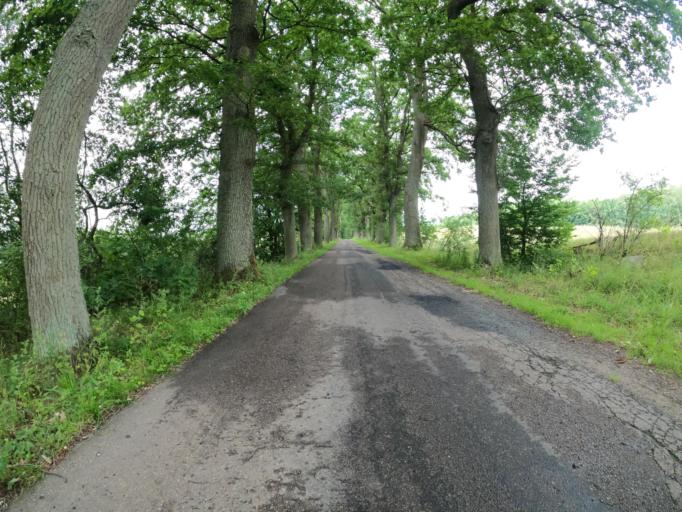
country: PL
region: West Pomeranian Voivodeship
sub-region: Powiat szczecinecki
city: Grzmiaca
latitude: 53.9280
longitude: 16.4804
